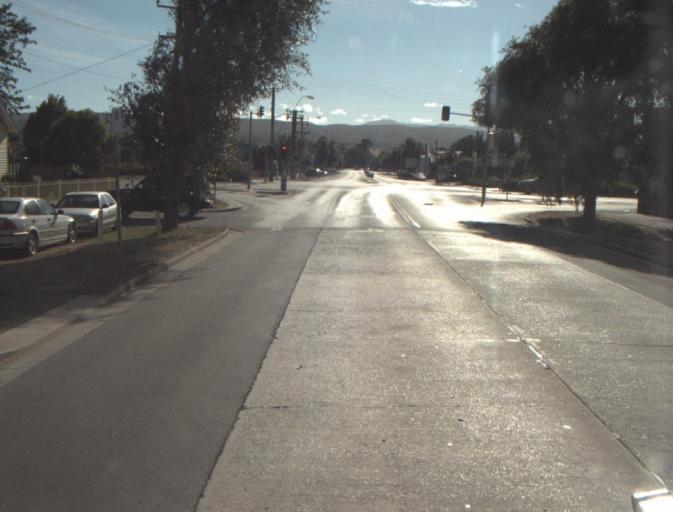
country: AU
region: Tasmania
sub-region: Launceston
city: Launceston
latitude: -41.4257
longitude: 147.1301
